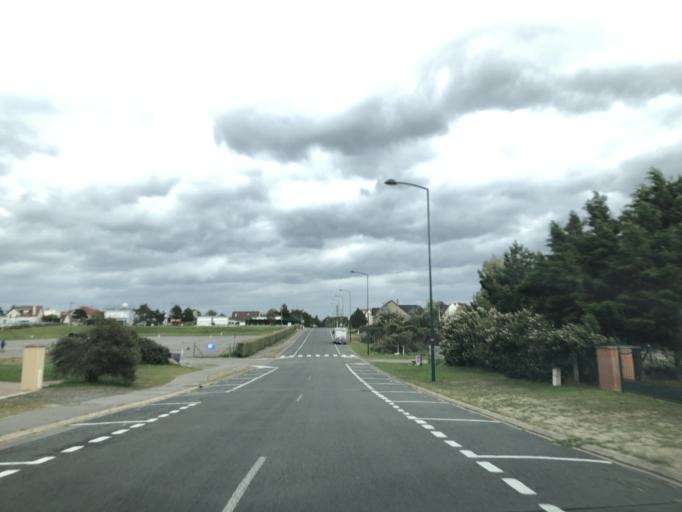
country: FR
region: Nord-Pas-de-Calais
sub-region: Departement du Pas-de-Calais
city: Cucq
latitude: 50.4794
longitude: 1.5835
